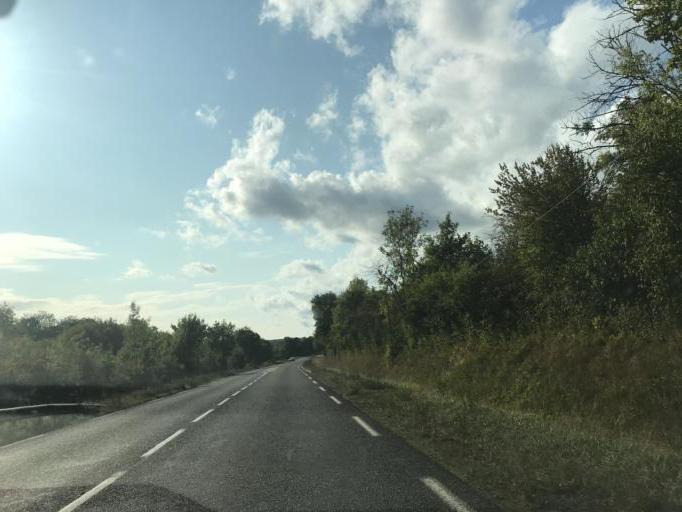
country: FR
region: Bourgogne
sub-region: Departement de l'Yonne
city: Avallon
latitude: 47.5218
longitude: 3.8025
